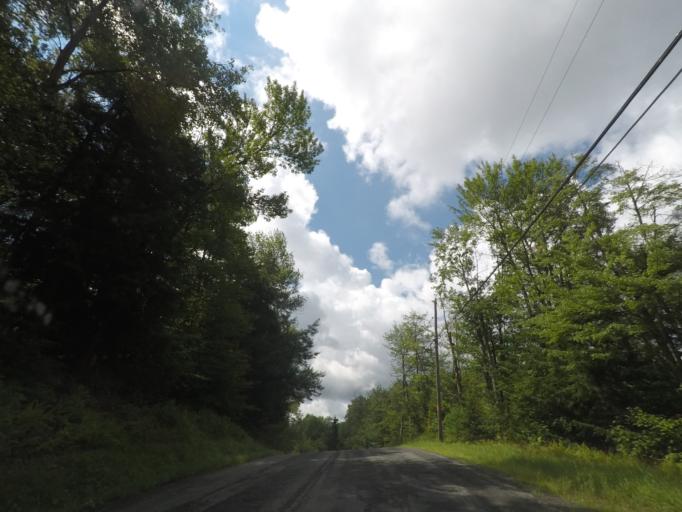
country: US
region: New York
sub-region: Rensselaer County
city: Averill Park
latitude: 42.6439
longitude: -73.4342
